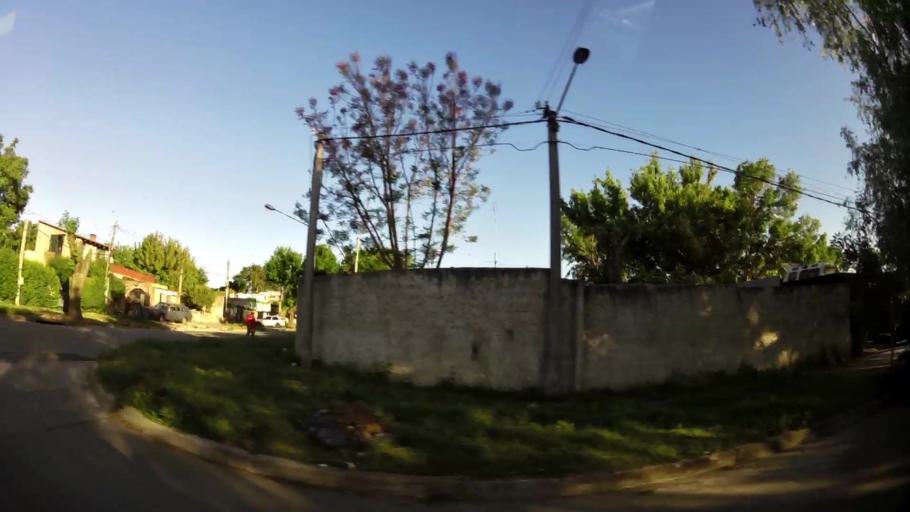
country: UY
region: Montevideo
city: Montevideo
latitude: -34.8453
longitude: -56.2142
